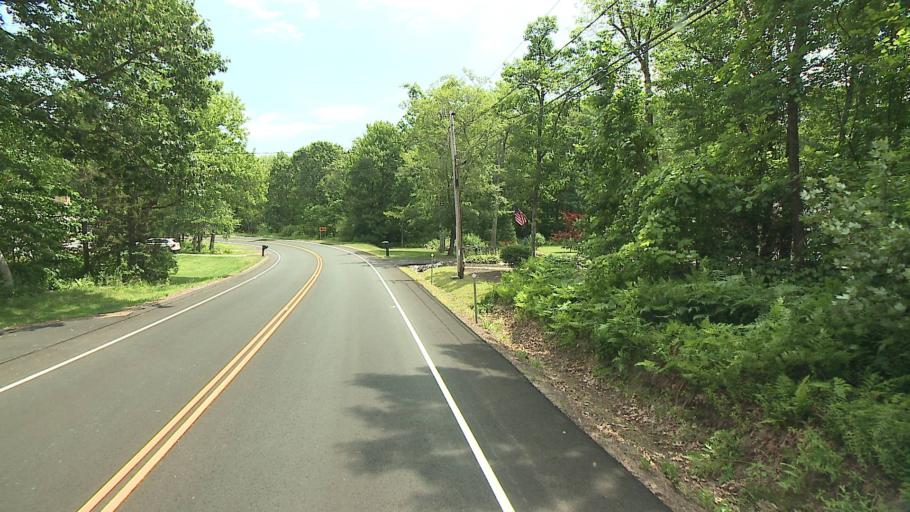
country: US
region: Connecticut
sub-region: Hartford County
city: North Granby
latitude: 41.9992
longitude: -72.8987
